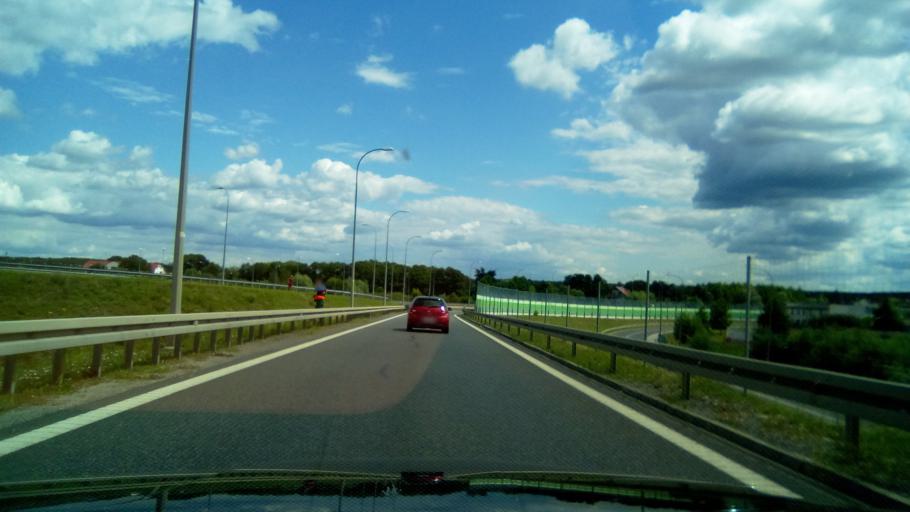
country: PL
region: Kujawsko-Pomorskie
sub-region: Powiat bydgoski
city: Biale Blota
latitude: 53.0931
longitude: 17.8949
